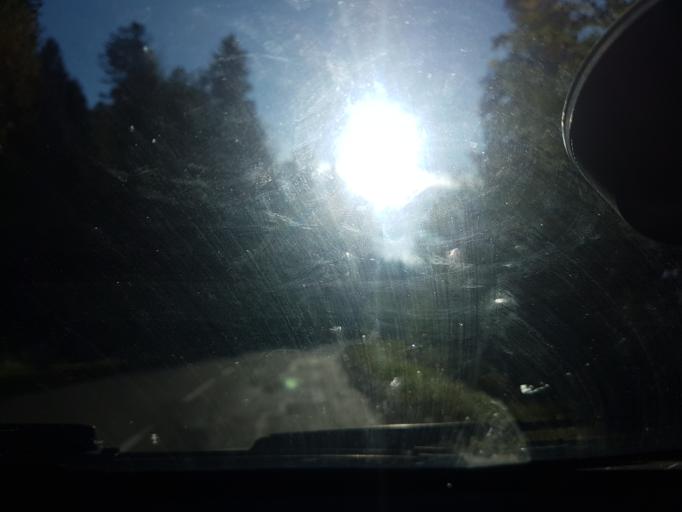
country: FR
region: Franche-Comte
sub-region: Departement de la Haute-Saone
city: Plancher-les-Mines
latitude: 47.7747
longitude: 6.7725
